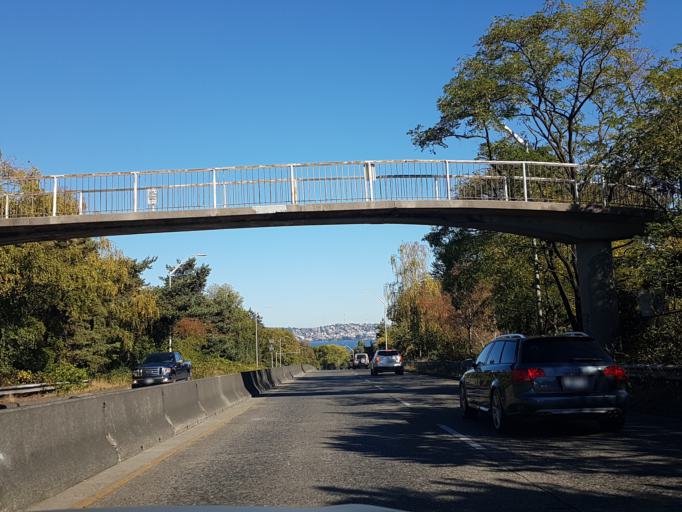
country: US
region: Washington
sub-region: King County
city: White Center
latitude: 47.5677
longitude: -122.3733
